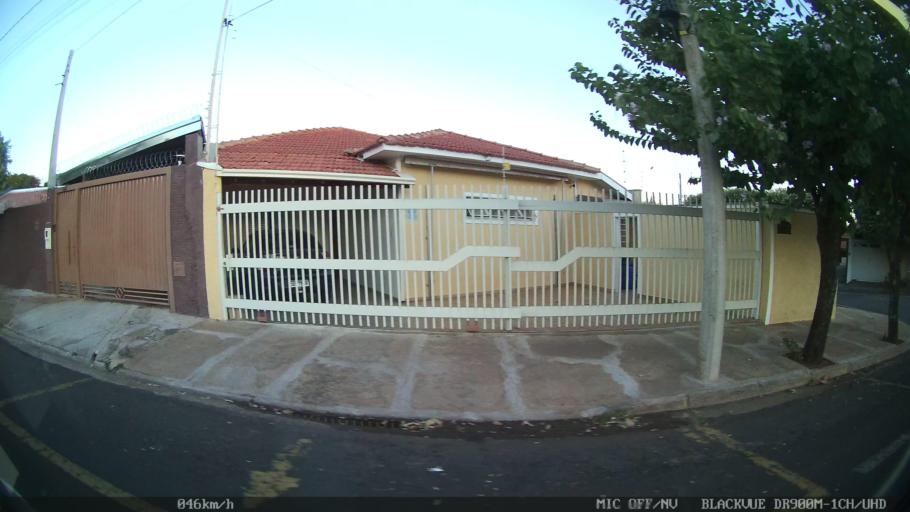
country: BR
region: Sao Paulo
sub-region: Sao Jose Do Rio Preto
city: Sao Jose do Rio Preto
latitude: -20.8432
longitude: -49.3757
